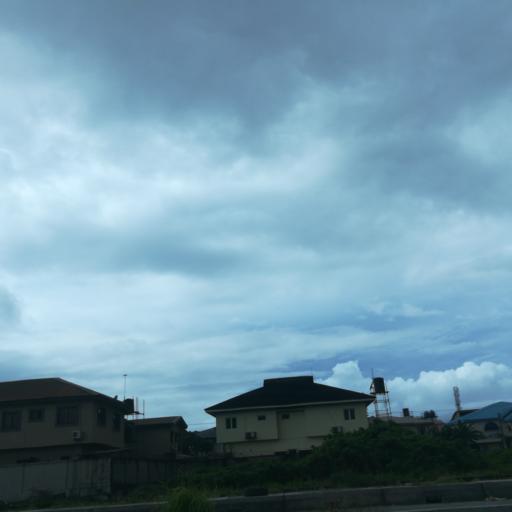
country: NG
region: Lagos
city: Ikoyi
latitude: 6.4372
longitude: 3.4598
